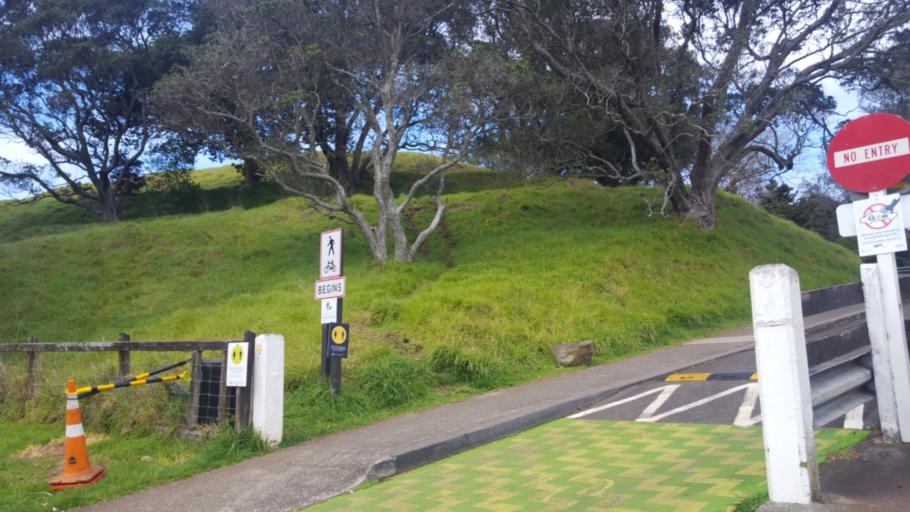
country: NZ
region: Auckland
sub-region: Auckland
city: Auckland
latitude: -36.8750
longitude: 174.7640
